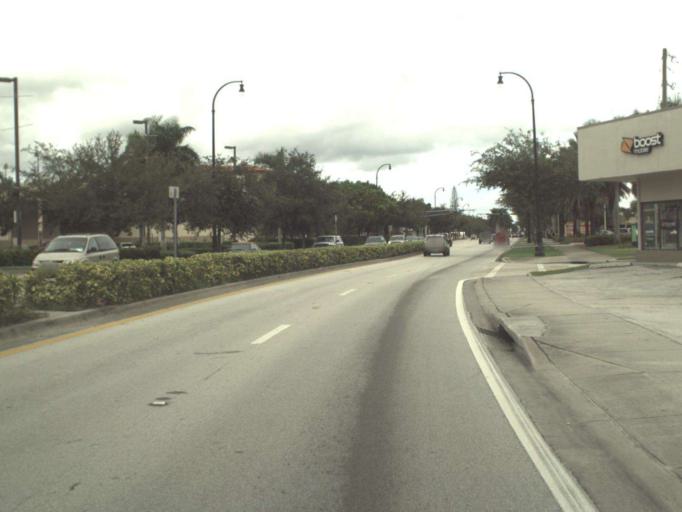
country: US
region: Florida
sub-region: Miami-Dade County
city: El Portal
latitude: 25.8574
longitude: -80.1845
